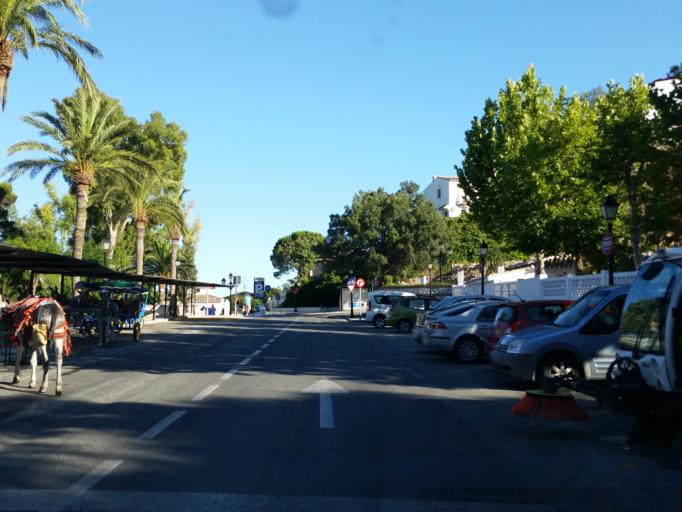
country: ES
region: Andalusia
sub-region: Provincia de Malaga
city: Mijas
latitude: 36.5959
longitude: -4.6368
